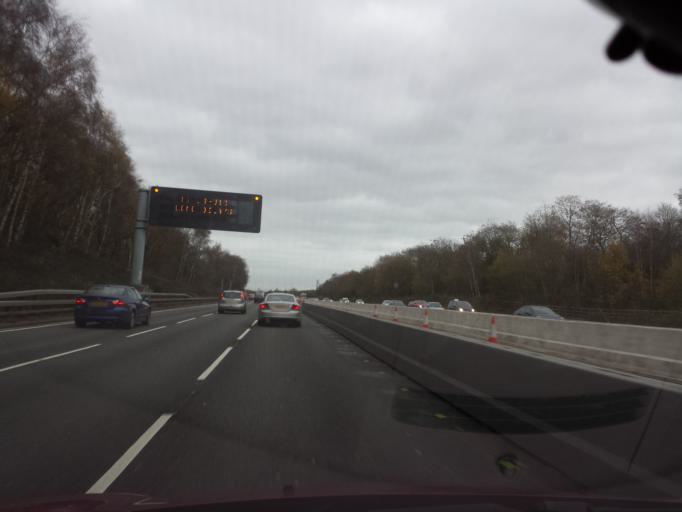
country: GB
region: England
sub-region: Surrey
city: Virginia Water
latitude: 51.3890
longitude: -0.5709
